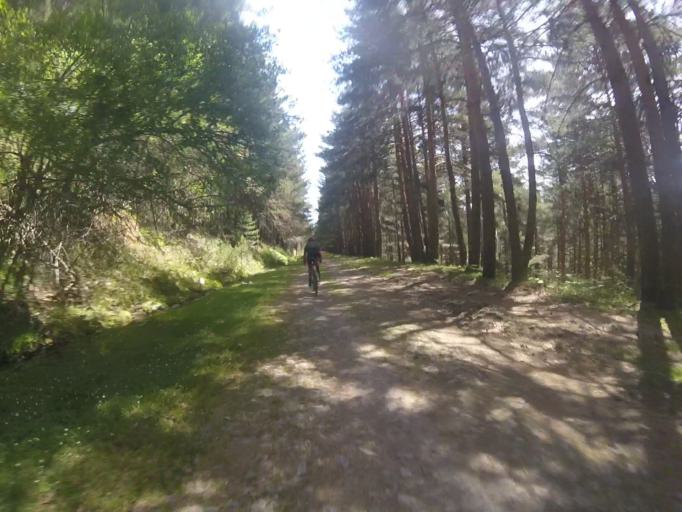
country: ES
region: Madrid
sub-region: Provincia de Madrid
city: Cercedilla
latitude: 40.8040
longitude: -4.0579
